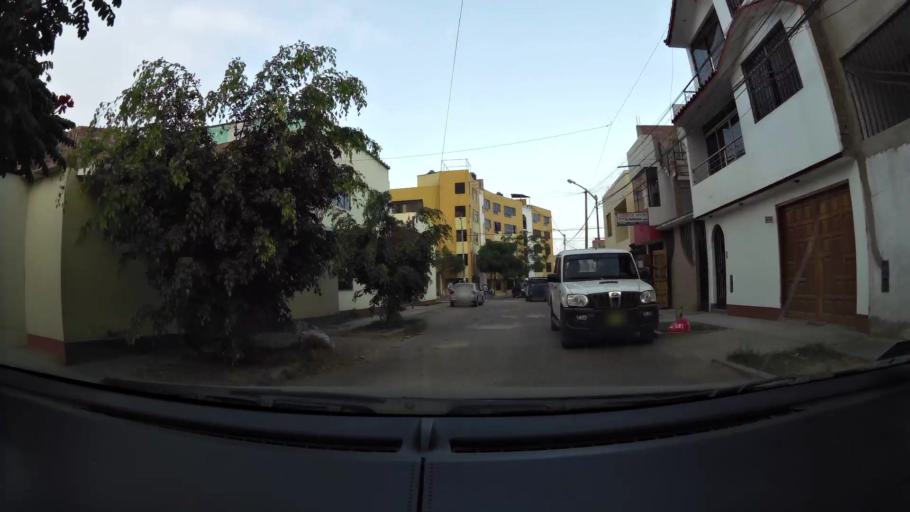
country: PE
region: La Libertad
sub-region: Provincia de Trujillo
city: Trujillo
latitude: -8.0990
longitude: -79.0415
